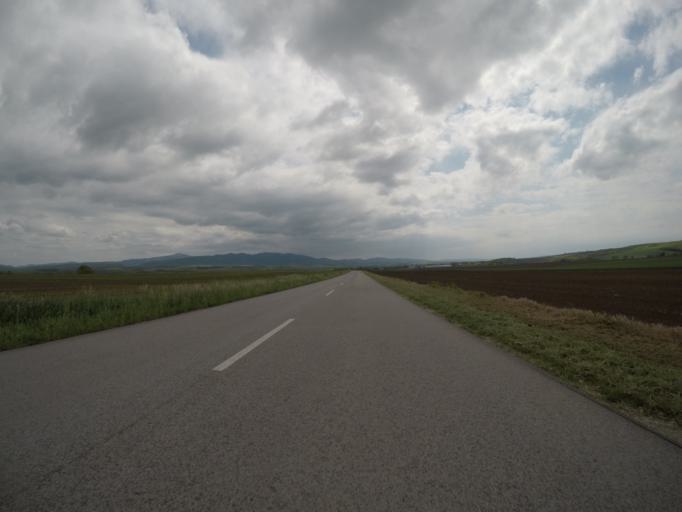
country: SK
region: Nitriansky
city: Zeliezovce
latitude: 48.0439
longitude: 18.7999
